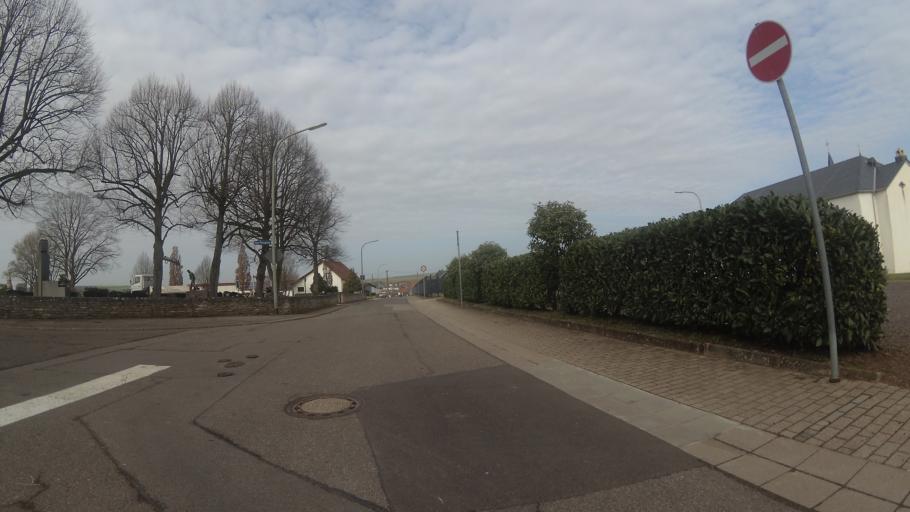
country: FR
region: Lorraine
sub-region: Departement de la Moselle
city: Merten
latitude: 49.2958
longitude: 6.6521
